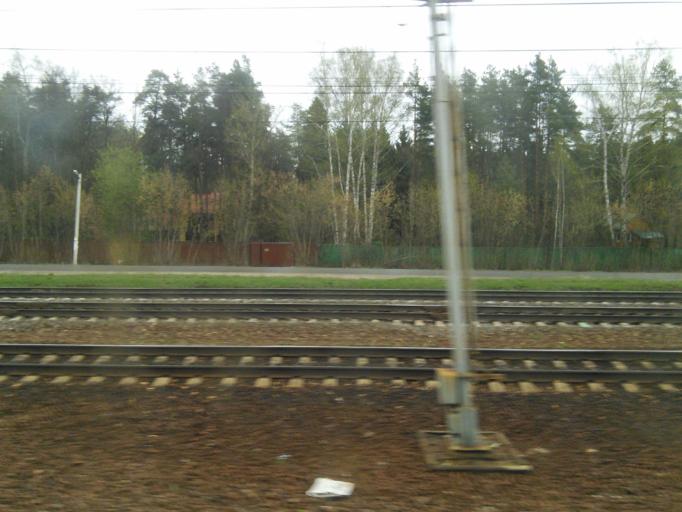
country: RU
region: Moskovskaya
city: Zhukovskiy
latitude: 55.6002
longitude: 38.1396
